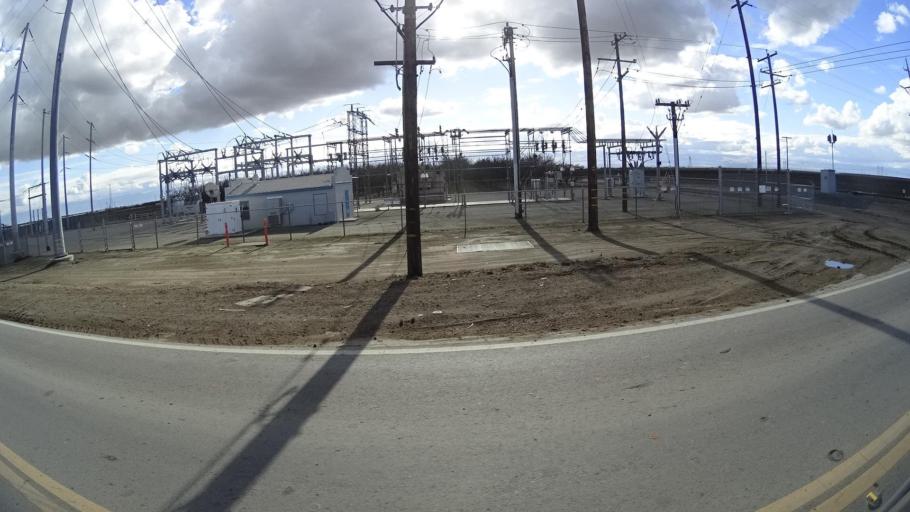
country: US
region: California
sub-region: Kern County
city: Greenfield
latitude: 35.2089
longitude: -119.1006
